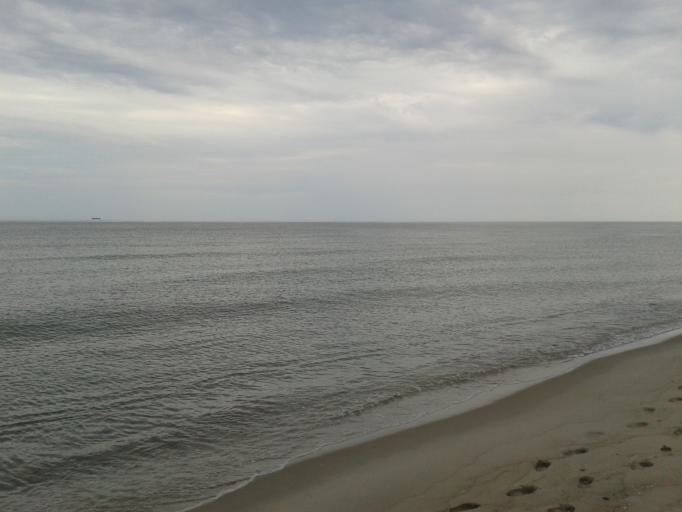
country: PL
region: Pomeranian Voivodeship
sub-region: Powiat pucki
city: Jastarnia
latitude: 54.7407
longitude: 18.5678
